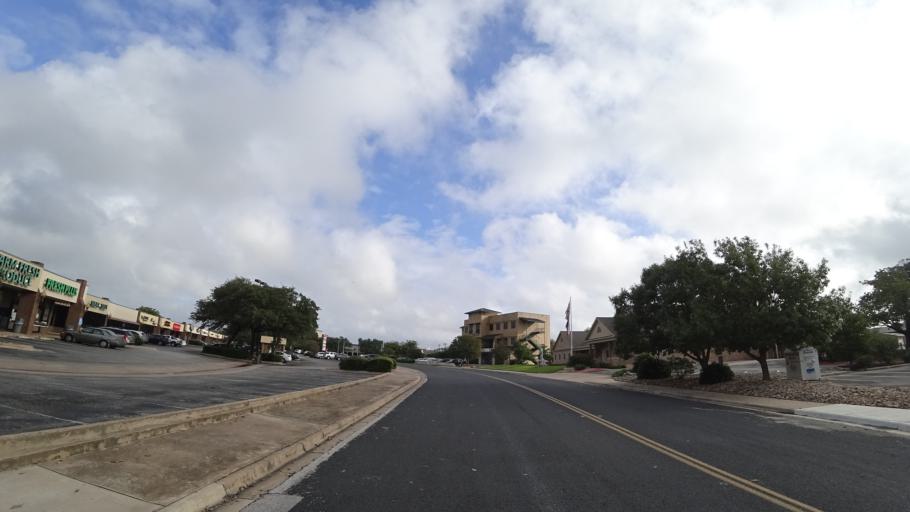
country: US
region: Texas
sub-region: Travis County
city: West Lake Hills
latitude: 30.3580
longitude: -97.7387
